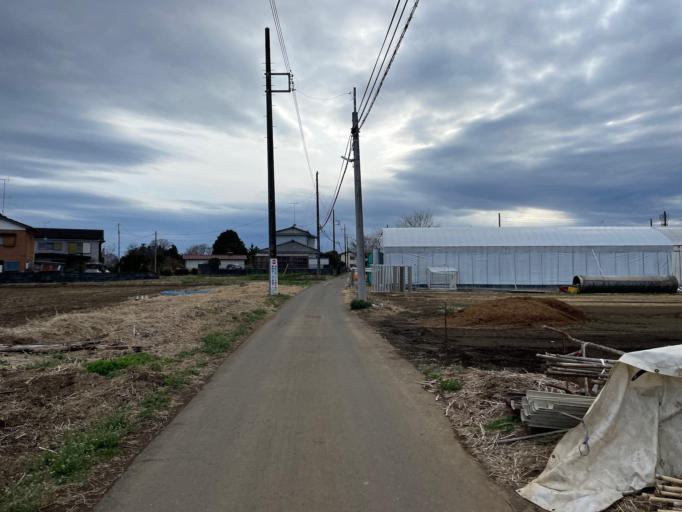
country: JP
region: Saitama
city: Sakado
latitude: 35.9430
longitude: 139.3500
